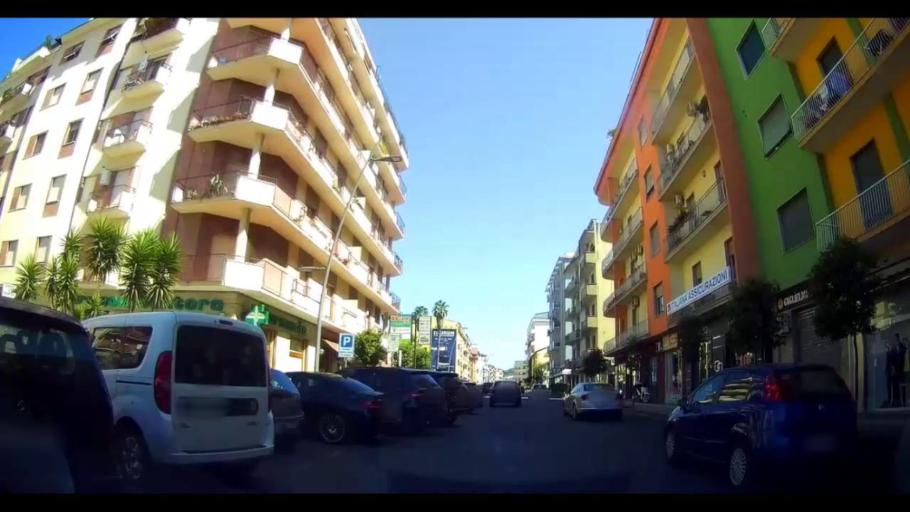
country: IT
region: Calabria
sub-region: Provincia di Cosenza
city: Cosenza
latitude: 39.3046
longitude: 16.2506
